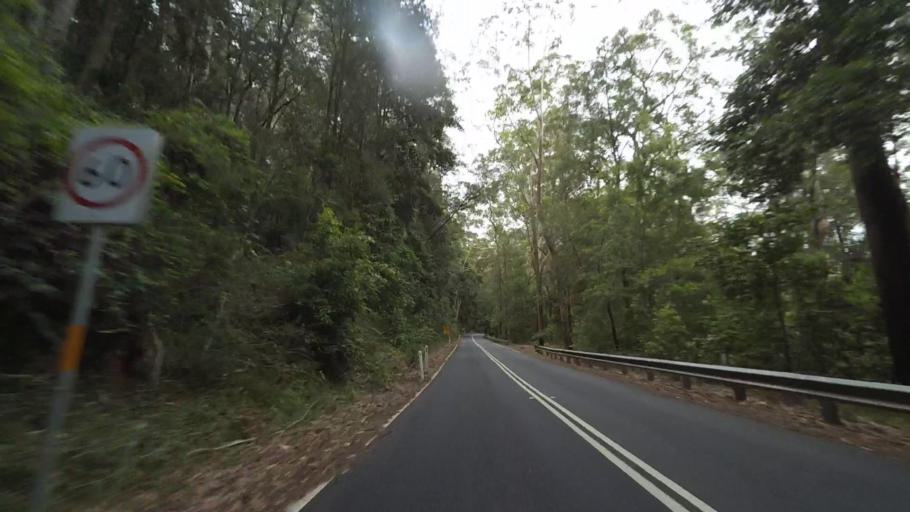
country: AU
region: New South Wales
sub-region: Wollongong
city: Helensburgh
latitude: -34.1520
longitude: 151.0328
